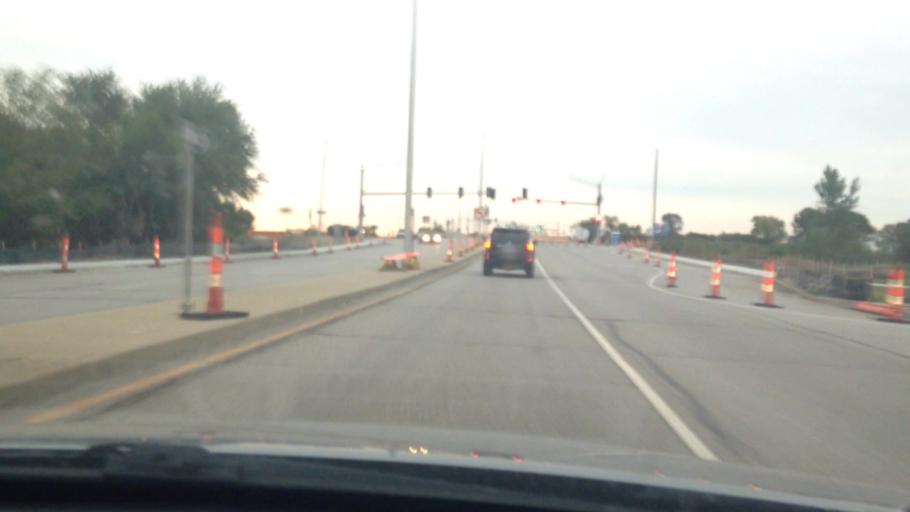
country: US
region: Missouri
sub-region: Jackson County
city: Lees Summit
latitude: 38.9425
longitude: -94.3782
